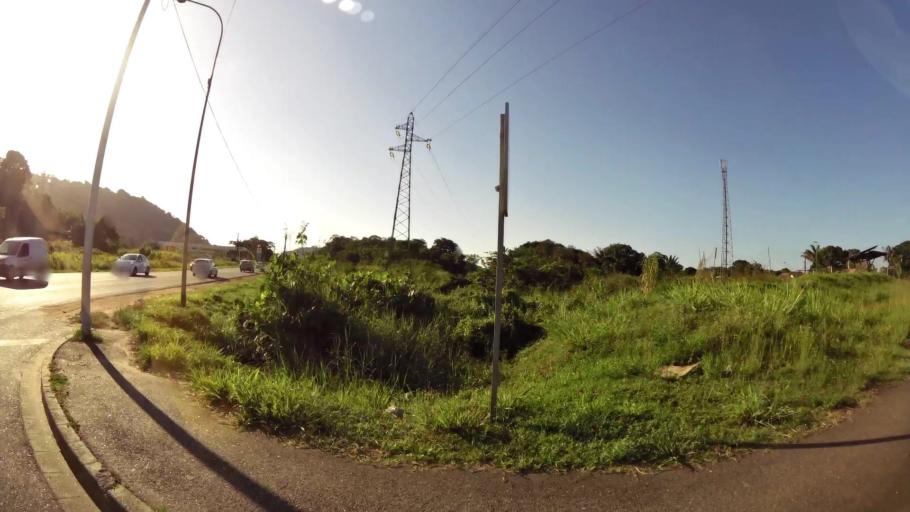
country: GF
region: Guyane
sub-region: Guyane
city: Remire-Montjoly
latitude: 4.8912
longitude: -52.2884
